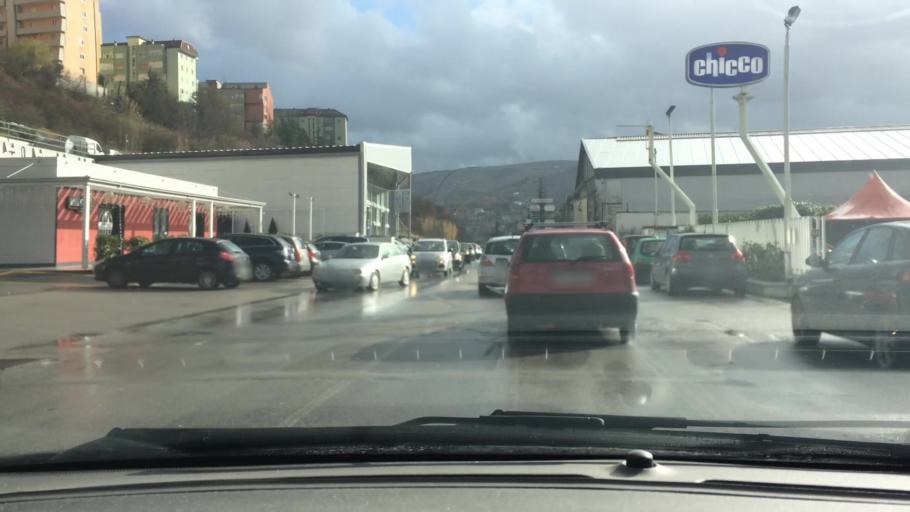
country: IT
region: Basilicate
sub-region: Provincia di Potenza
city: Potenza
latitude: 40.6316
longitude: 15.7895
